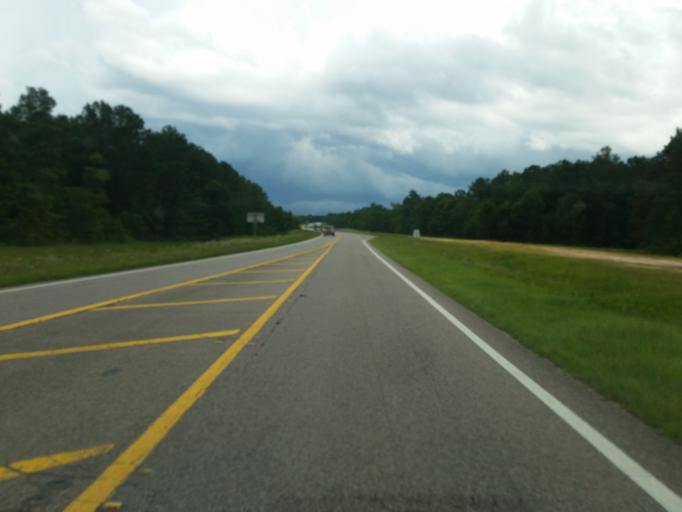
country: US
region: Mississippi
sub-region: George County
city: Lucedale
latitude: 30.8659
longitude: -88.4227
